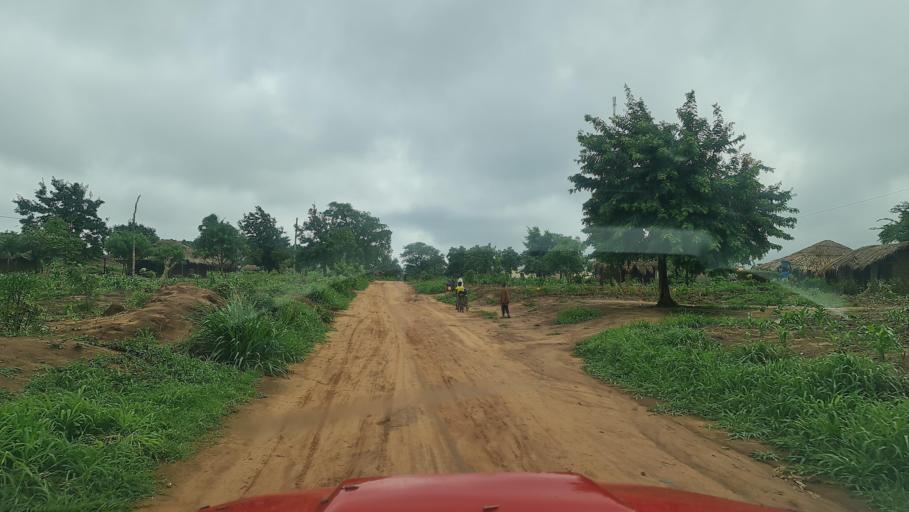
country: MW
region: Southern Region
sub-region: Nsanje District
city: Nsanje
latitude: -17.1913
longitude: 35.7061
